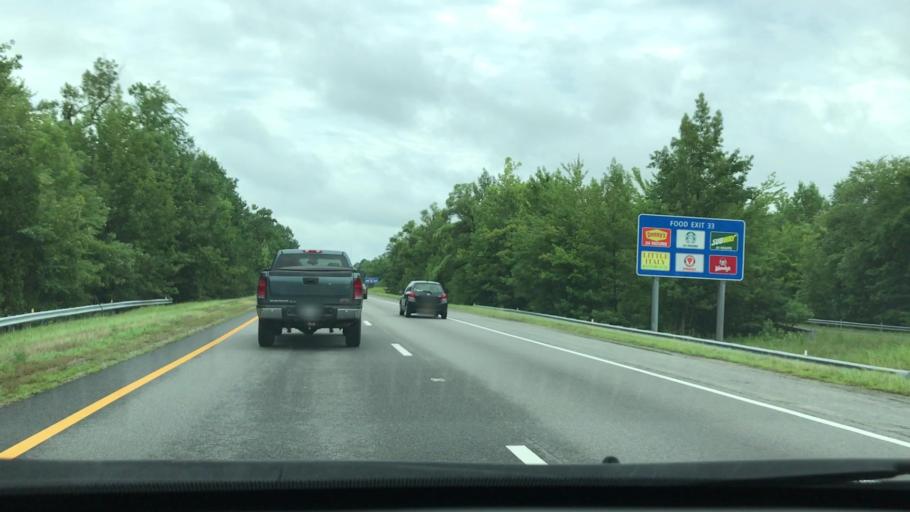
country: US
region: Virginia
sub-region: Sussex County
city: Sussex
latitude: 36.9667
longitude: -77.3922
